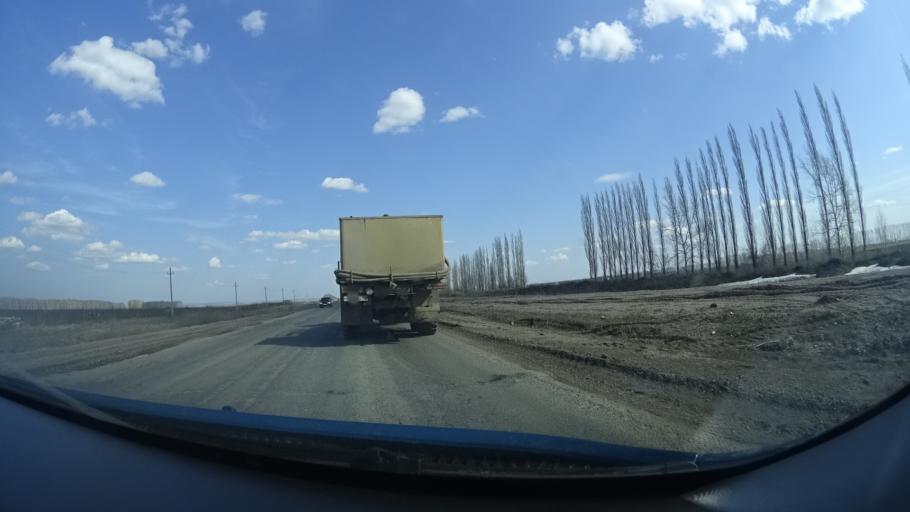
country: RU
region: Bashkortostan
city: Buzdyak
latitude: 54.6421
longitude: 54.5266
